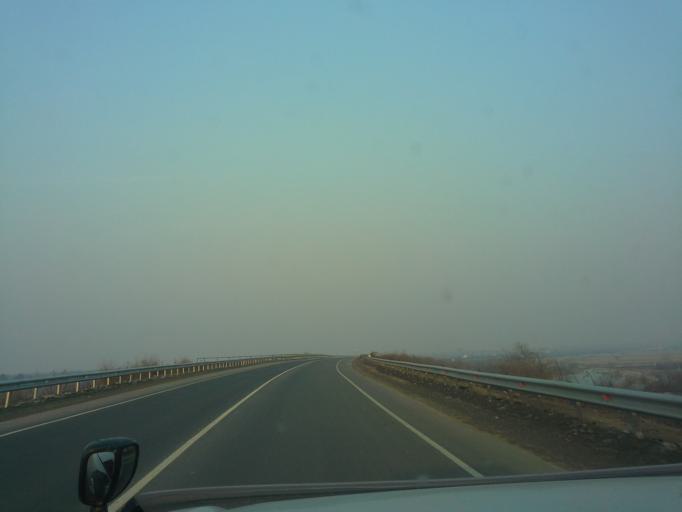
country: RU
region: Jewish Autonomous Oblast
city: Priamurskiy
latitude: 48.5210
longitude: 134.9151
